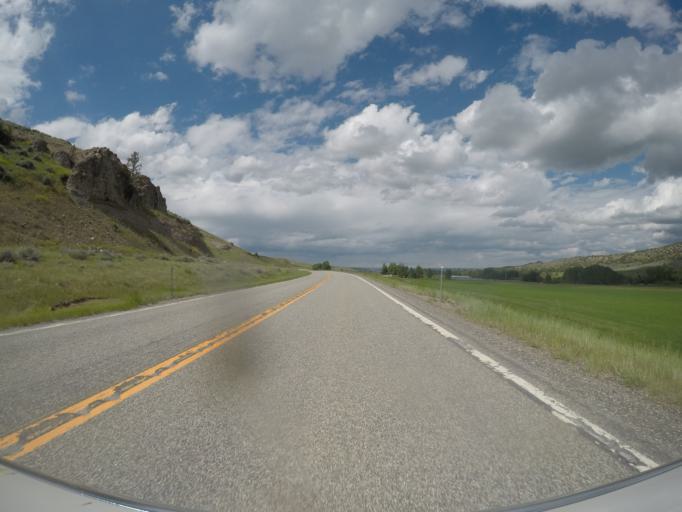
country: US
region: Montana
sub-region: Sweet Grass County
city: Big Timber
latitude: 45.7483
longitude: -109.9942
